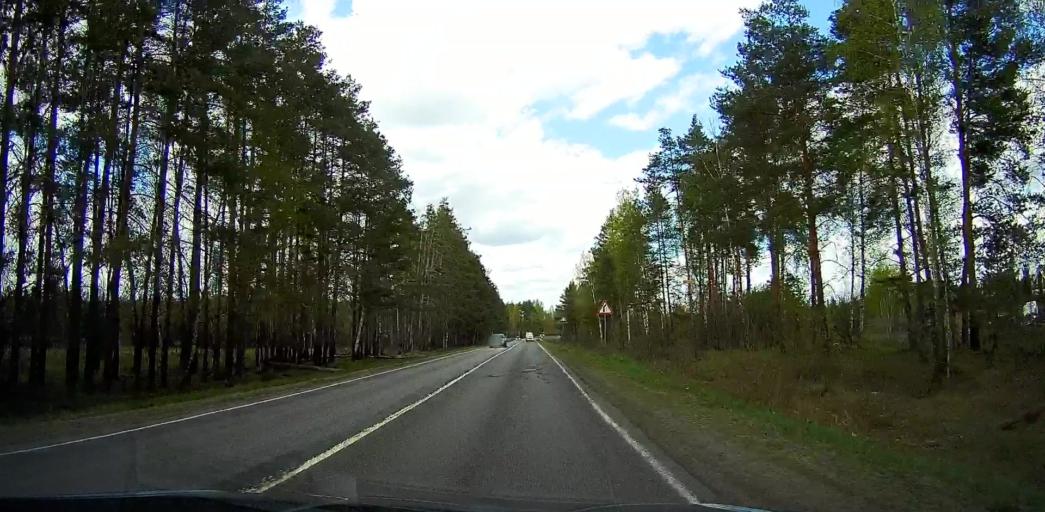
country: RU
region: Moskovskaya
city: Davydovo
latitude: 55.6273
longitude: 38.8615
